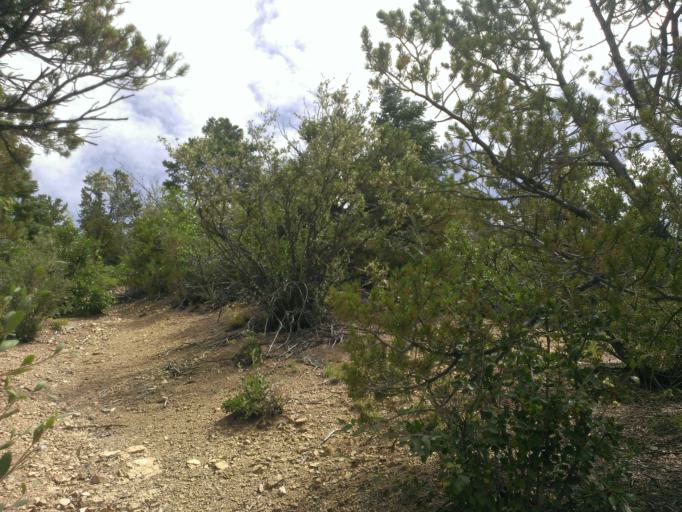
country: US
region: New Mexico
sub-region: Taos County
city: Arroyo Seco
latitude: 36.5373
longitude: -105.5542
